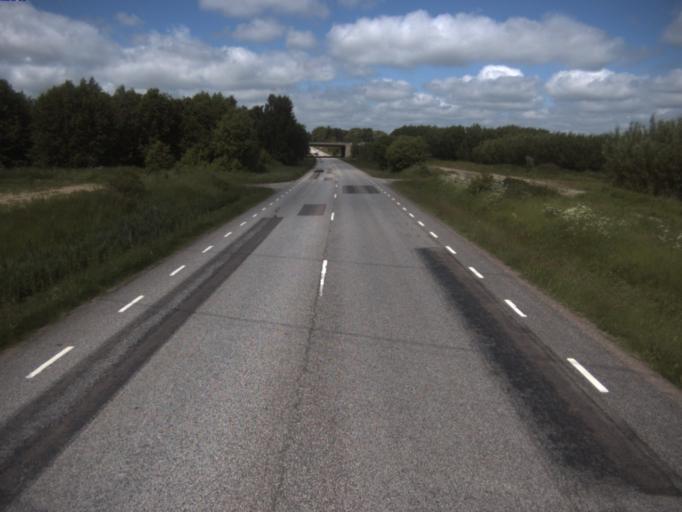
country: SE
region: Skane
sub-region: Helsingborg
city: Odakra
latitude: 56.0842
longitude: 12.7655
